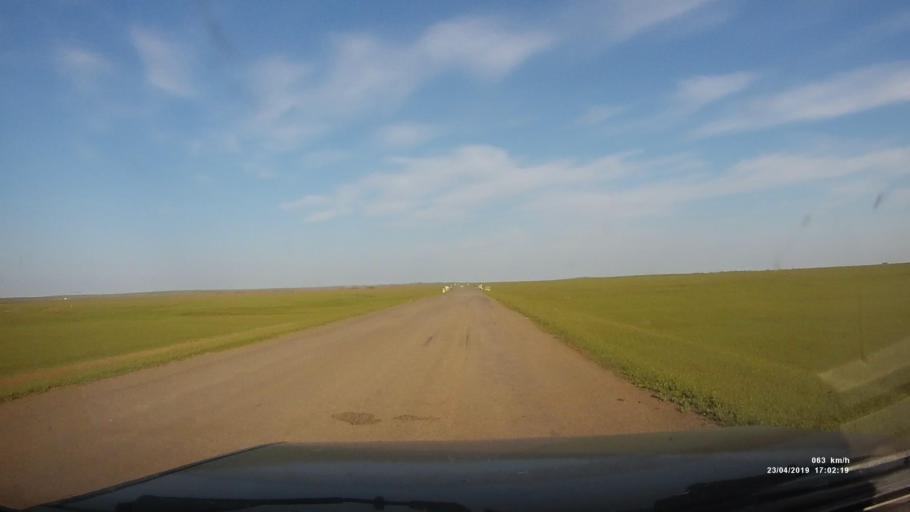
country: RU
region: Kalmykiya
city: Priyutnoye
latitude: 46.2929
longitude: 43.4164
